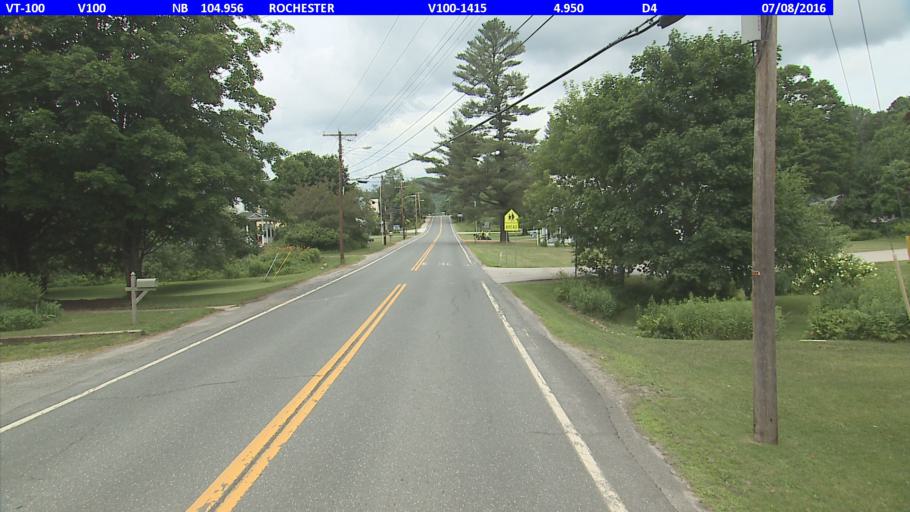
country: US
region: Vermont
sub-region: Orange County
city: Randolph
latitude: 43.8696
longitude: -72.8079
